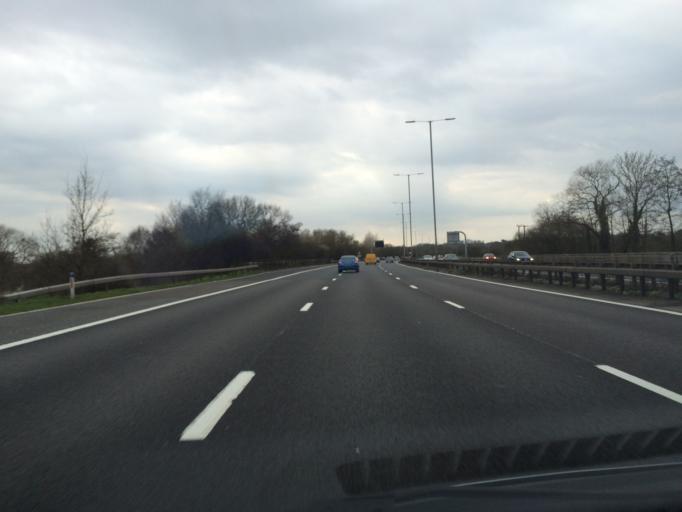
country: GB
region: England
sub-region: Wokingham
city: Lower Earley
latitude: 51.4202
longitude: -0.9099
